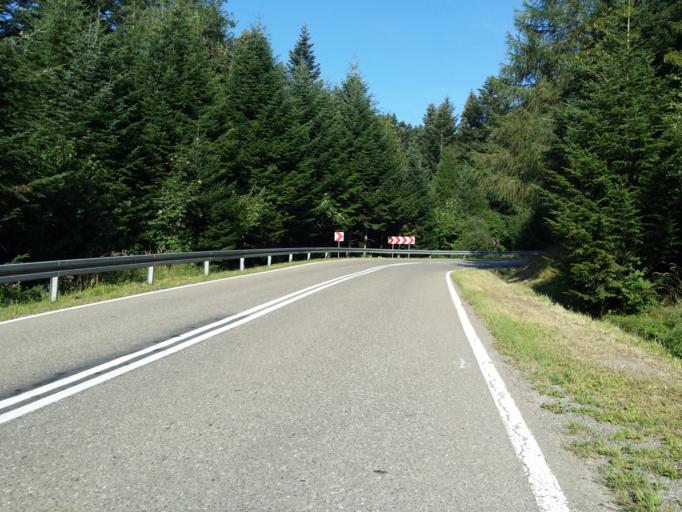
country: PL
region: Subcarpathian Voivodeship
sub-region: Powiat leski
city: Cisna
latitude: 49.2367
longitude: 22.3004
